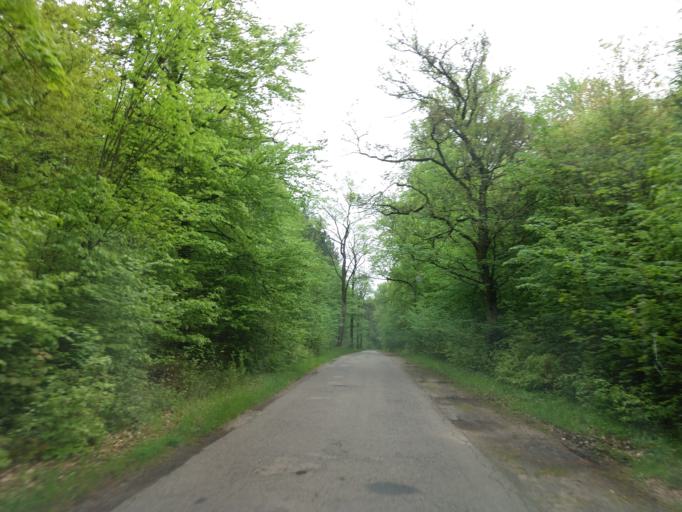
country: PL
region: West Pomeranian Voivodeship
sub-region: Powiat choszczenski
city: Krzecin
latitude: 53.0458
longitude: 15.5672
